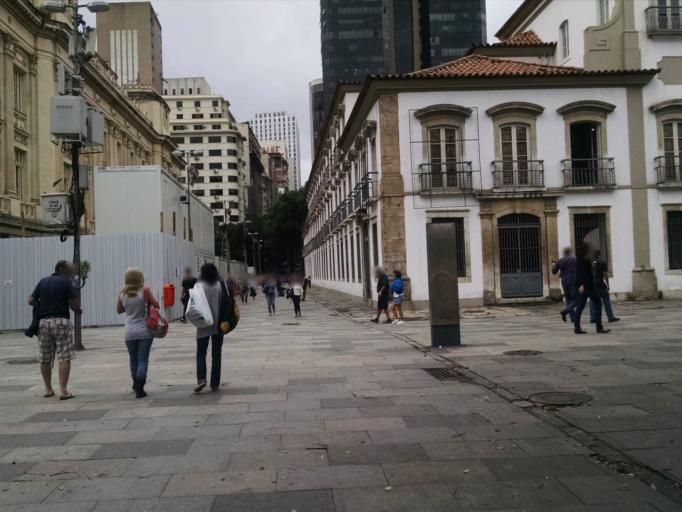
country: BR
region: Rio de Janeiro
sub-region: Rio De Janeiro
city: Rio de Janeiro
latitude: -22.9033
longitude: -43.1736
